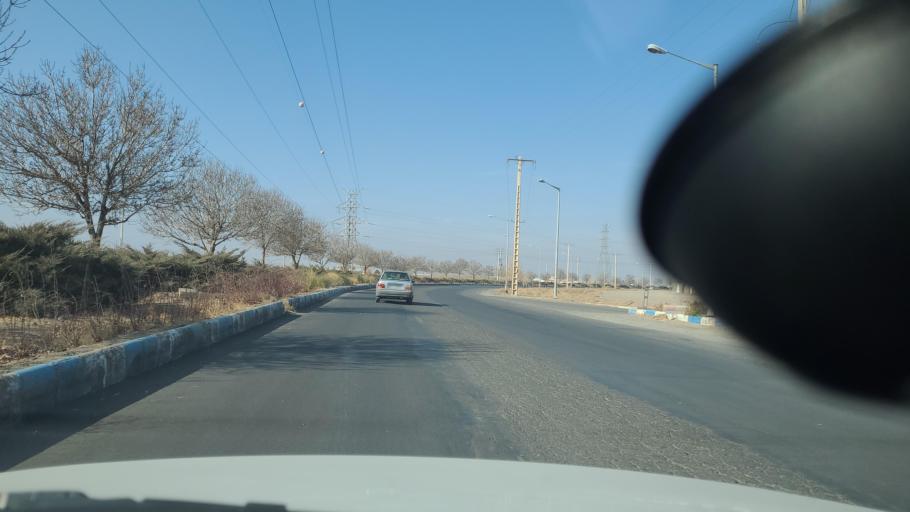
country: IR
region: Razavi Khorasan
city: Fariman
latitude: 35.6989
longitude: 59.8373
